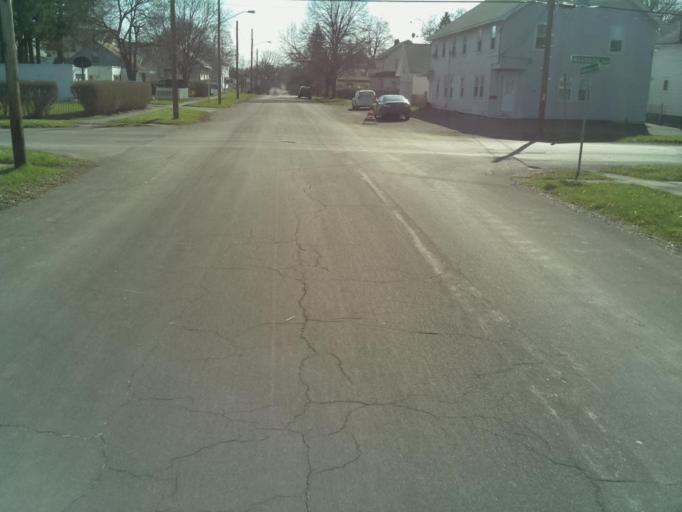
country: US
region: New York
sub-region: Onondaga County
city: Lyncourt
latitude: 43.0639
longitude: -76.1092
